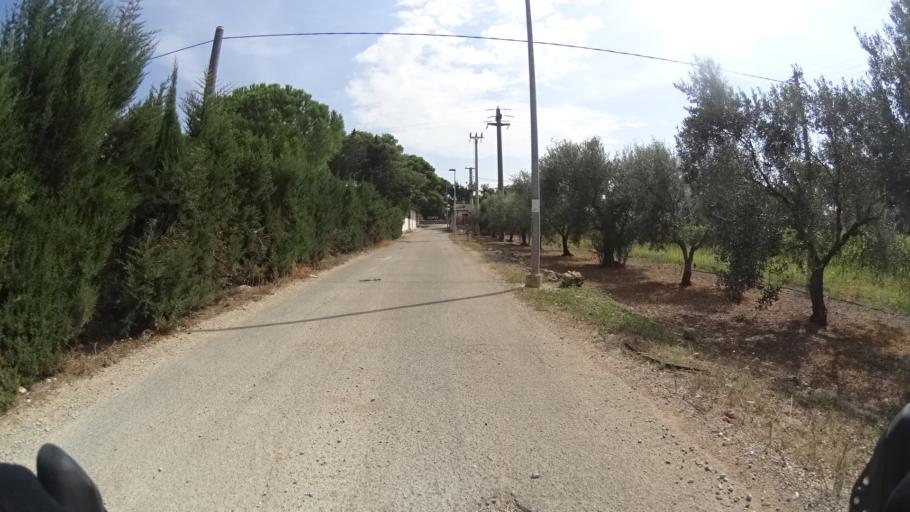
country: IT
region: Apulia
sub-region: Provincia di Lecce
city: Porto Cesareo
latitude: 40.2753
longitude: 17.9327
